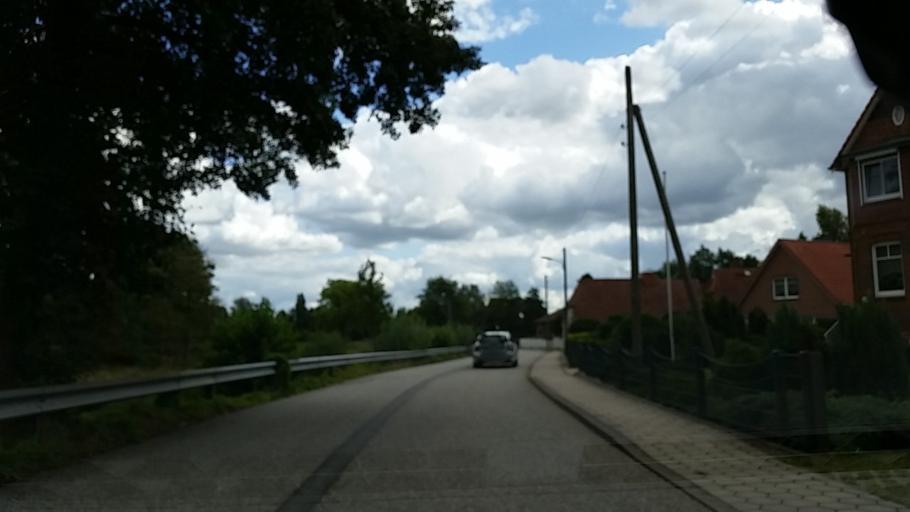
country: DE
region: Schleswig-Holstein
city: Escheburg
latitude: 53.4504
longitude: 10.2894
